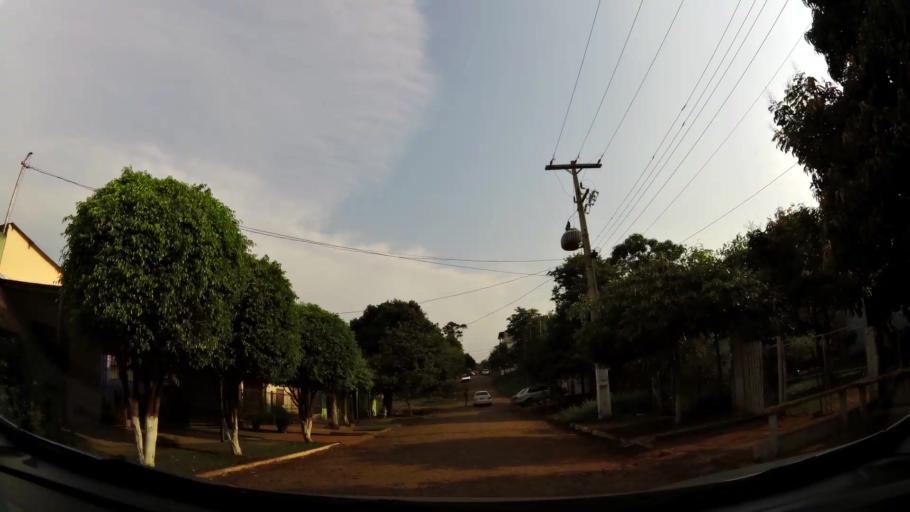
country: PY
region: Alto Parana
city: Ciudad del Este
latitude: -25.4816
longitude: -54.6716
